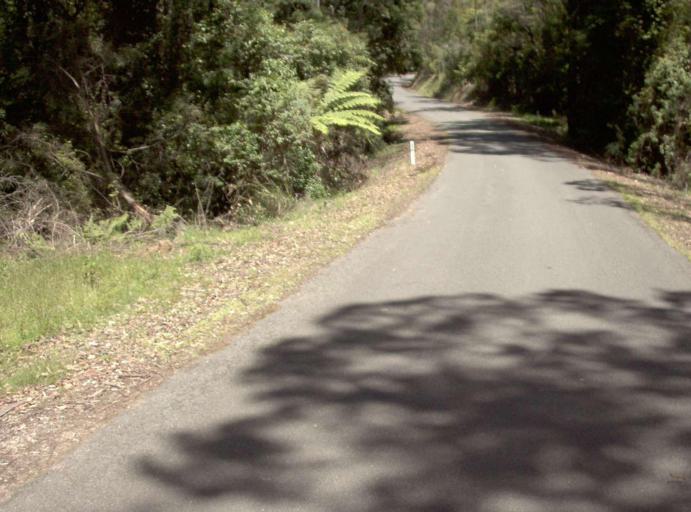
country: AU
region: New South Wales
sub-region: Bombala
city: Bombala
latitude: -37.4935
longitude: 148.9254
